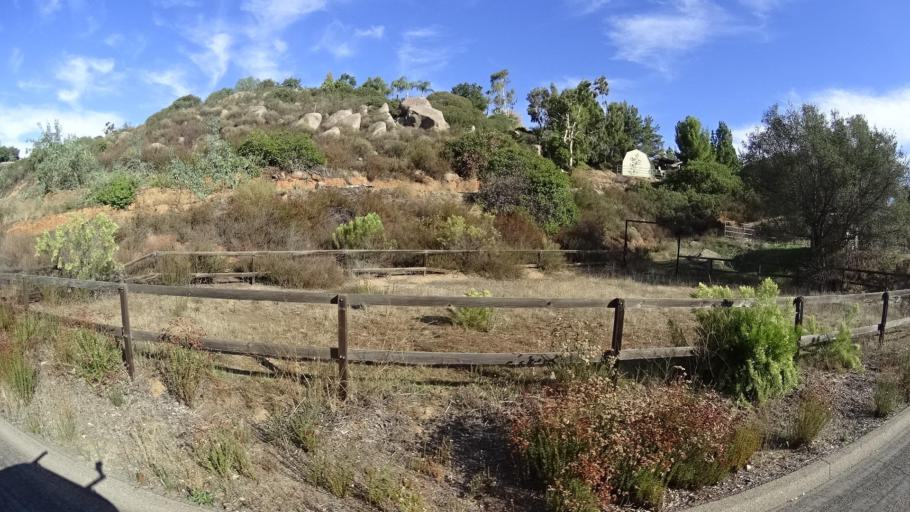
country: US
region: California
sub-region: San Diego County
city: Alpine
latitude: 32.8148
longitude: -116.7474
